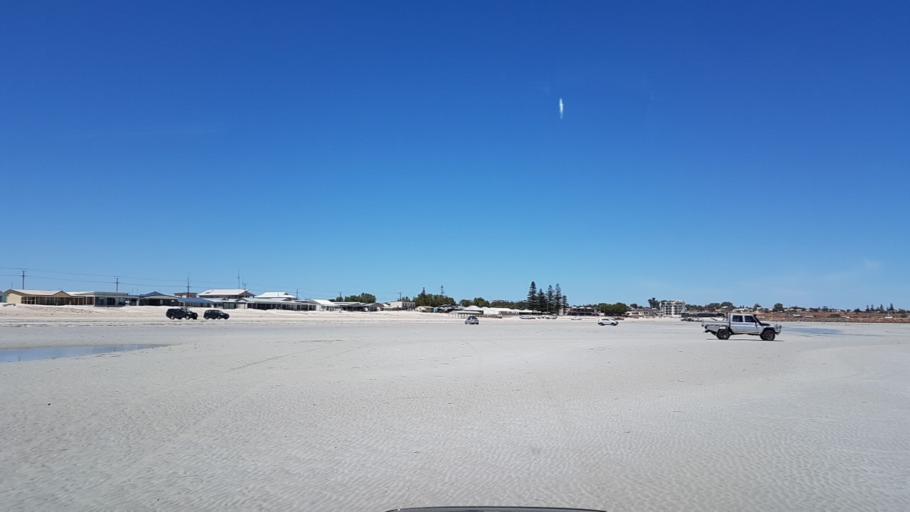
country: AU
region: South Australia
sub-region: Copper Coast
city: Wallaroo
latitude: -33.9153
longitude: 137.6301
